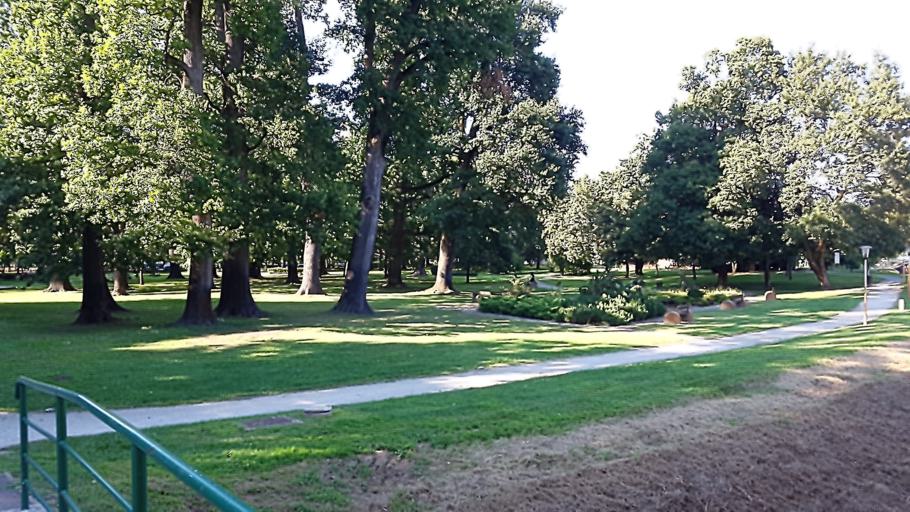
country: SI
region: Ljutomer
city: Ljutomer
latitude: 46.5196
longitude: 16.1928
